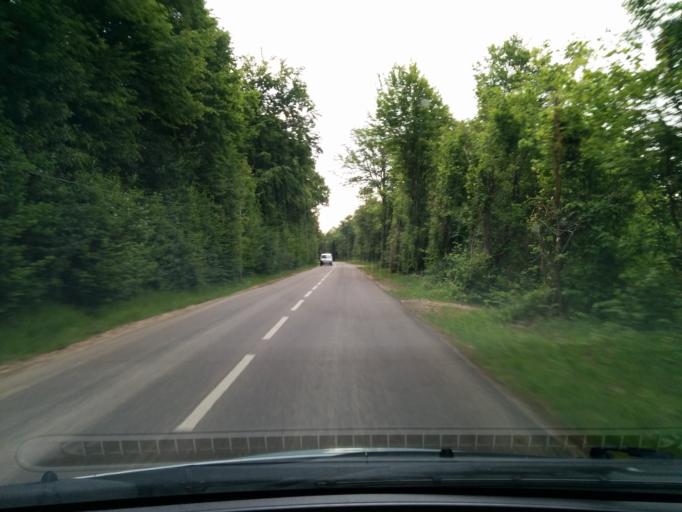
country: FR
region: Haute-Normandie
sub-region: Departement de l'Eure
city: Gasny
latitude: 49.0862
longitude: 1.6389
